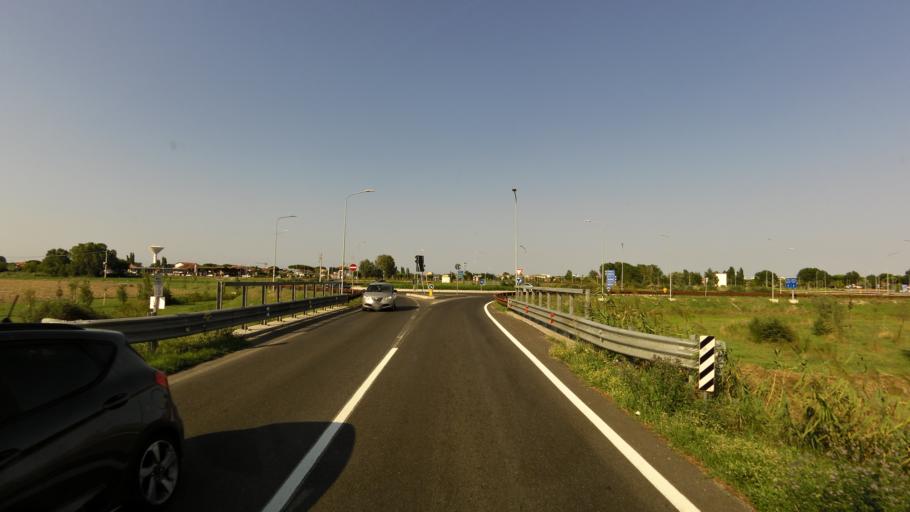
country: IT
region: Emilia-Romagna
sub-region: Provincia di Ravenna
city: Cervia
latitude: 44.2319
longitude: 12.3581
